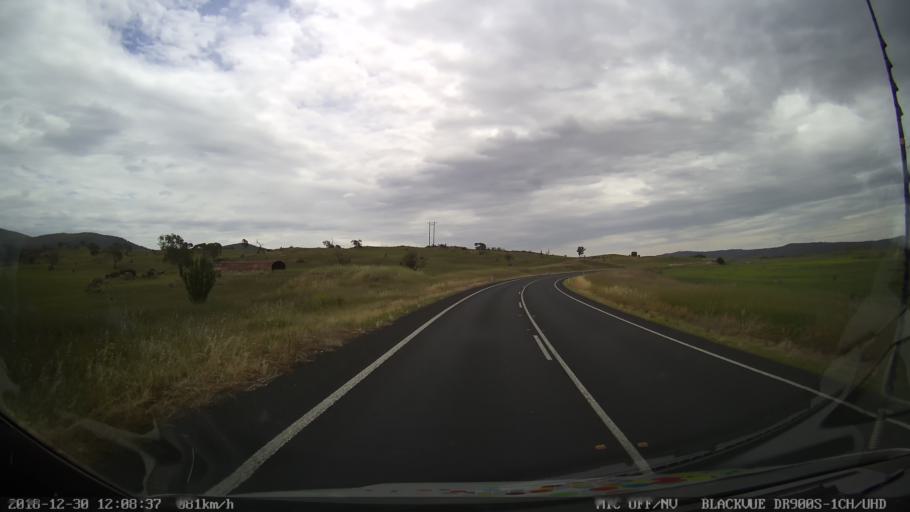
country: AU
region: New South Wales
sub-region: Snowy River
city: Jindabyne
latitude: -36.3930
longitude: 148.5941
